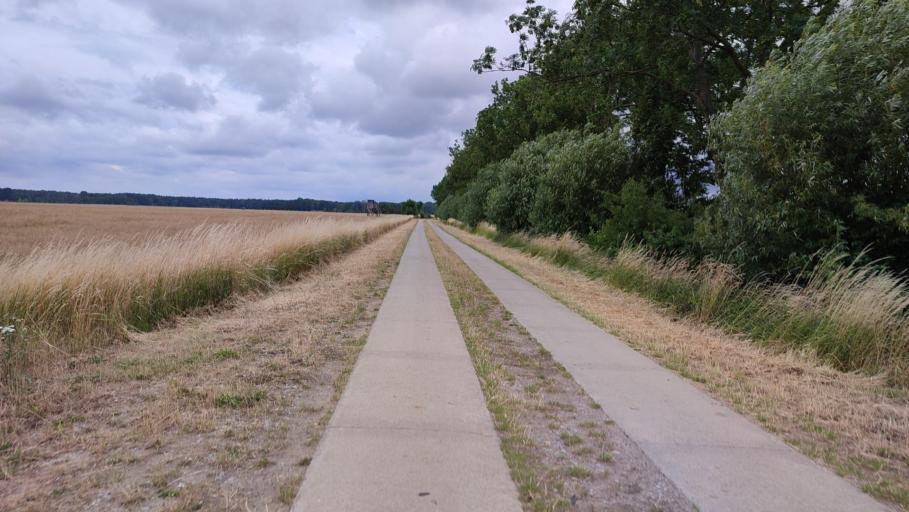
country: DE
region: Lower Saxony
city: Hitzacker
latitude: 53.1723
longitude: 11.1019
